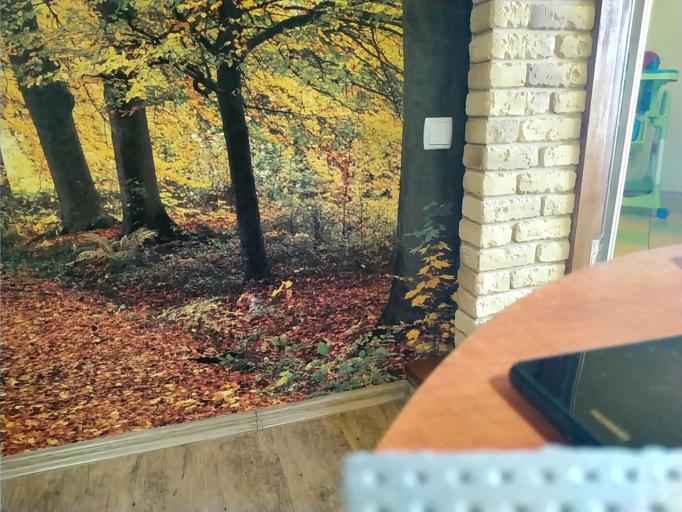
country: RU
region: Kaluga
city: Kondrovo
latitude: 54.7982
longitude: 35.8994
